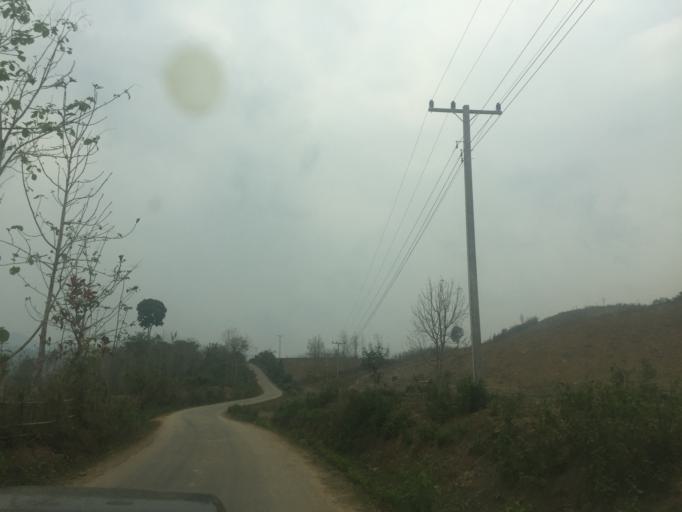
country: LA
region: Vientiane
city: Muang Sanakham
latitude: 18.3805
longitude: 101.5449
